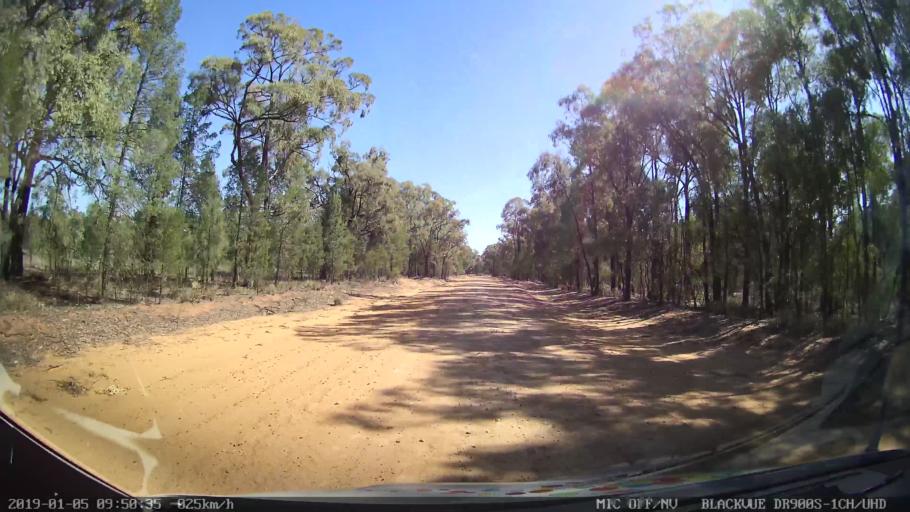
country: AU
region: New South Wales
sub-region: Gilgandra
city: Gilgandra
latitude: -31.6640
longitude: 148.7590
